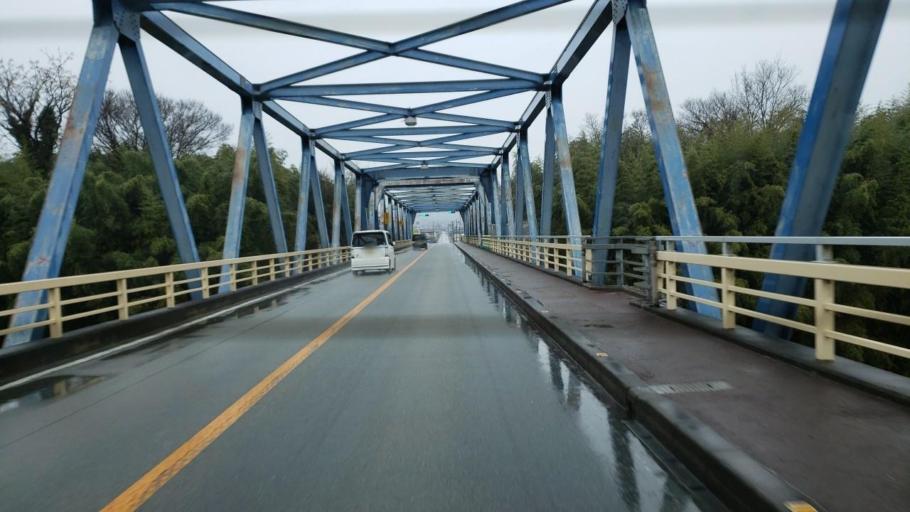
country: JP
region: Tokushima
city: Kamojimacho-jogejima
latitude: 34.0731
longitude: 134.2811
